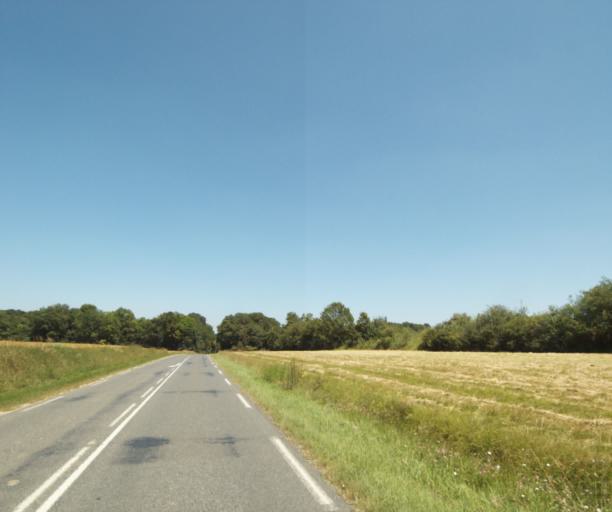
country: FR
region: Ile-de-France
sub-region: Departement de l'Essonne
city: Milly-la-Foret
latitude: 48.3573
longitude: 2.4585
